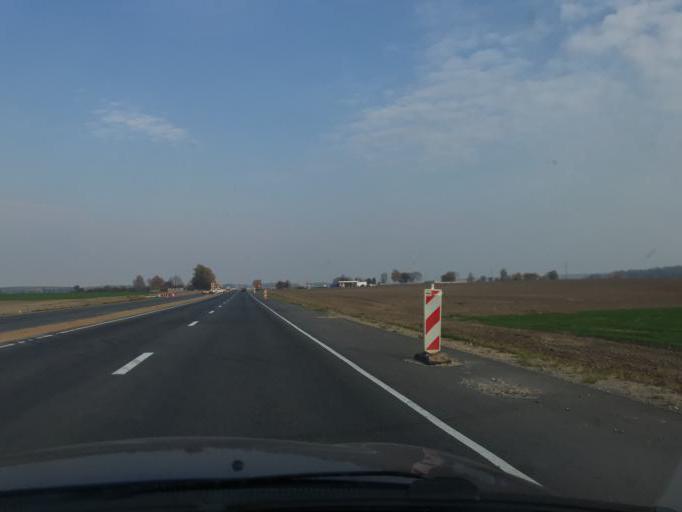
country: BY
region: Grodnenskaya
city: Shchuchin
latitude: 53.7238
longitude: 24.9689
